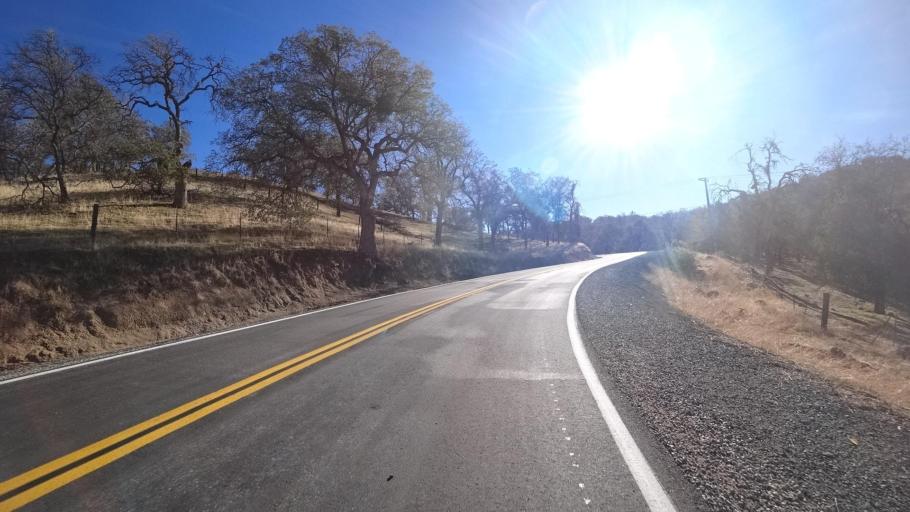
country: US
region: California
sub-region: Kern County
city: Alta Sierra
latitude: 35.7059
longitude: -118.7627
